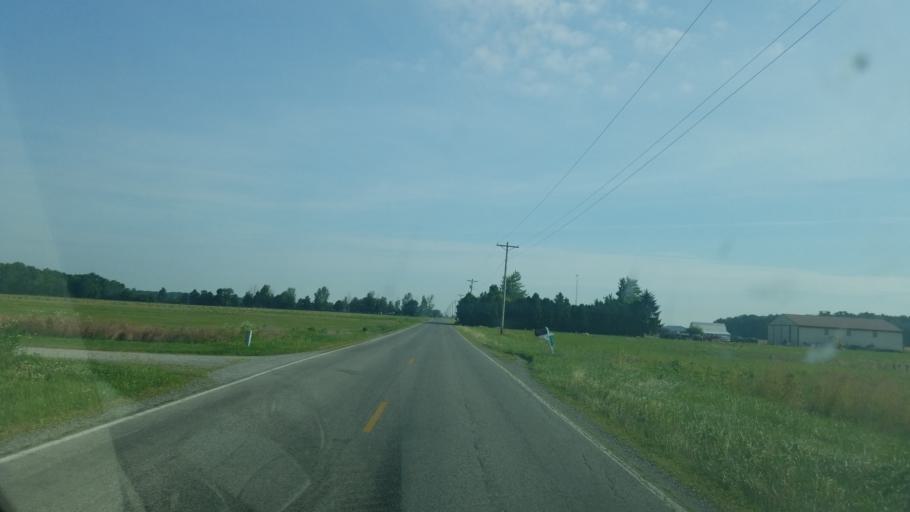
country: US
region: Ohio
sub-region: Hancock County
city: Arlington
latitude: 40.9385
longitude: -83.6987
